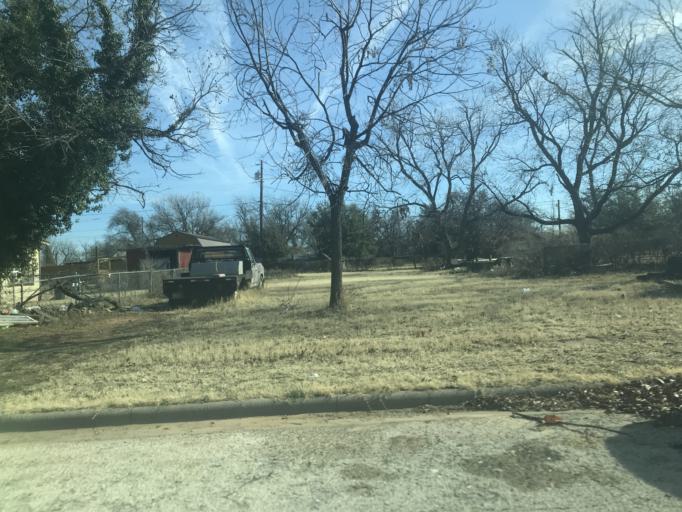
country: US
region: Texas
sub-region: Taylor County
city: Abilene
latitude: 32.4888
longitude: -99.7361
